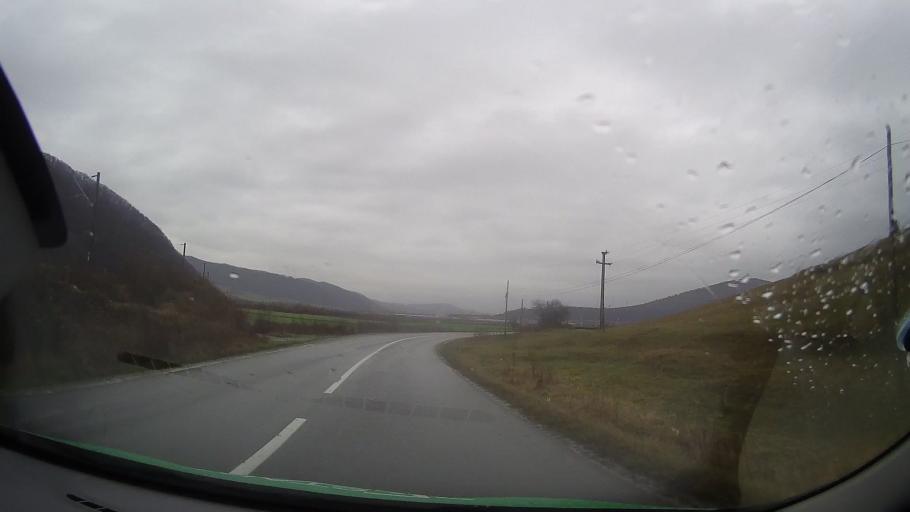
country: RO
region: Bistrita-Nasaud
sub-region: Municipiul Bistrita
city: Viisoara
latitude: 47.0568
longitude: 24.4398
